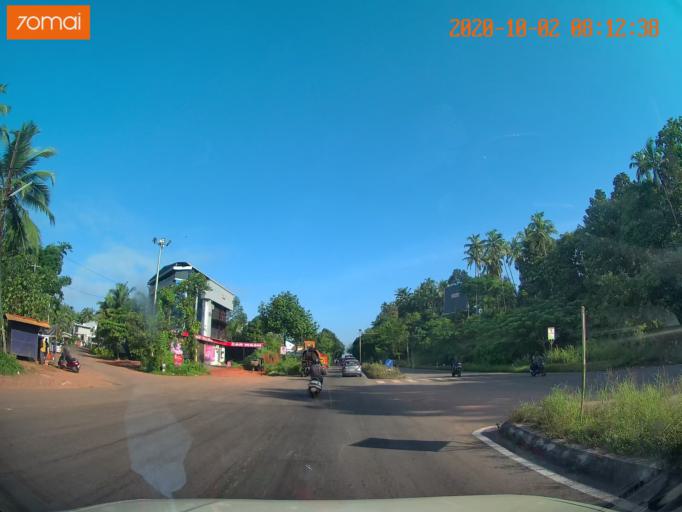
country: IN
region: Kerala
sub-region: Kozhikode
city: Kozhikode
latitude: 11.2831
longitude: 75.8027
